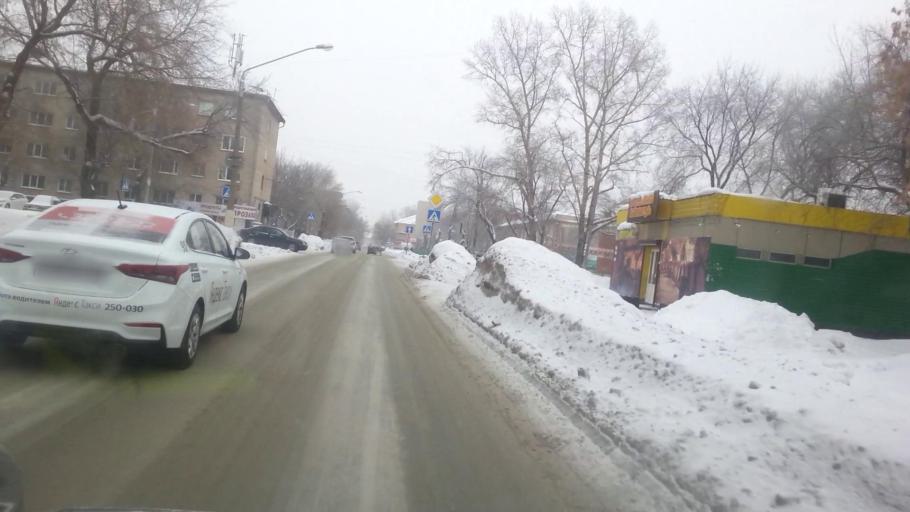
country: RU
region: Altai Krai
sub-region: Gorod Barnaulskiy
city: Barnaul
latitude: 53.3793
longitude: 83.7208
